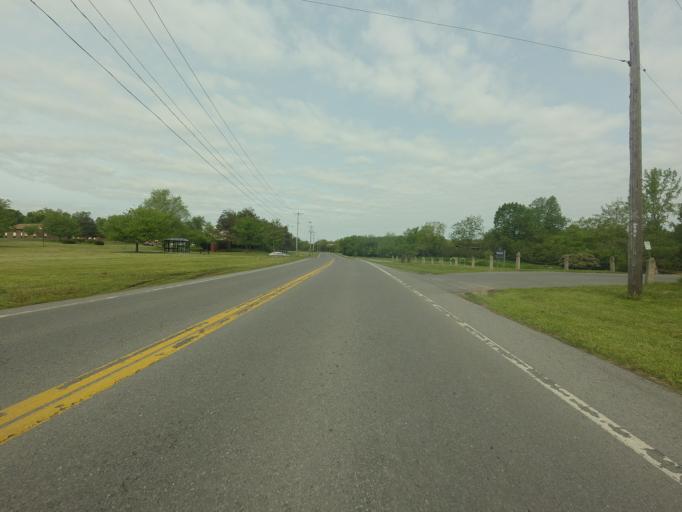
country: US
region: New York
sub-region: Jefferson County
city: Watertown
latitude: 43.9775
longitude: -75.8802
